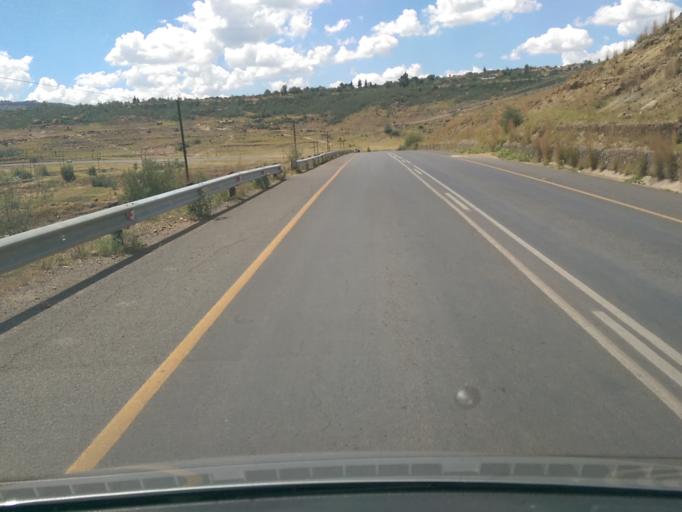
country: LS
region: Maseru
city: Maseru
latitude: -29.3849
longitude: 27.5032
